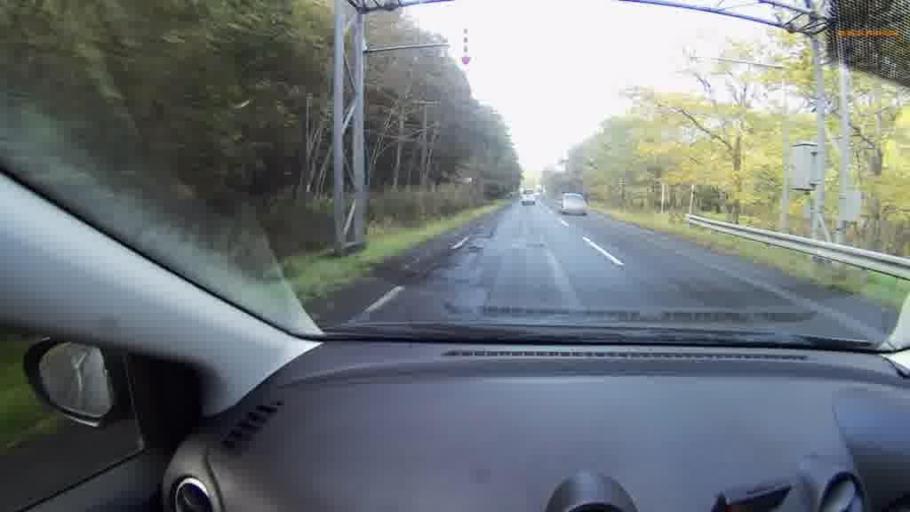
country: JP
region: Hokkaido
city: Kushiro
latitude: 42.9985
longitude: 144.4970
